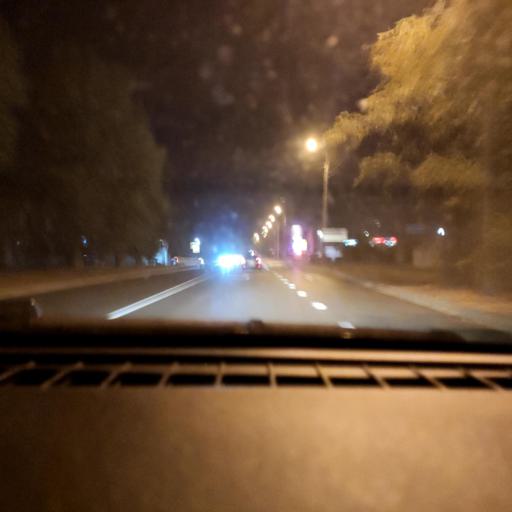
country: RU
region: Voronezj
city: Voronezh
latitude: 51.6561
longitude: 39.2482
